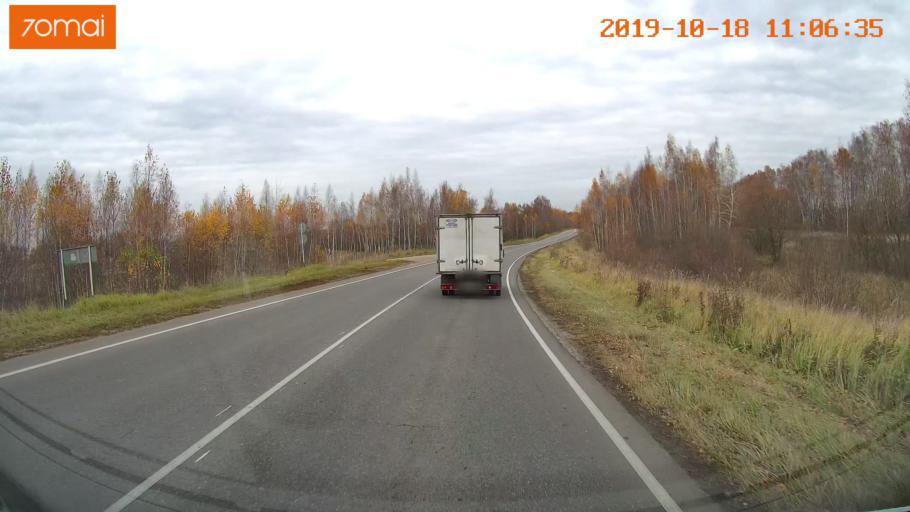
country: RU
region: Tula
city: Kimovsk
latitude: 53.9193
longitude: 38.5350
